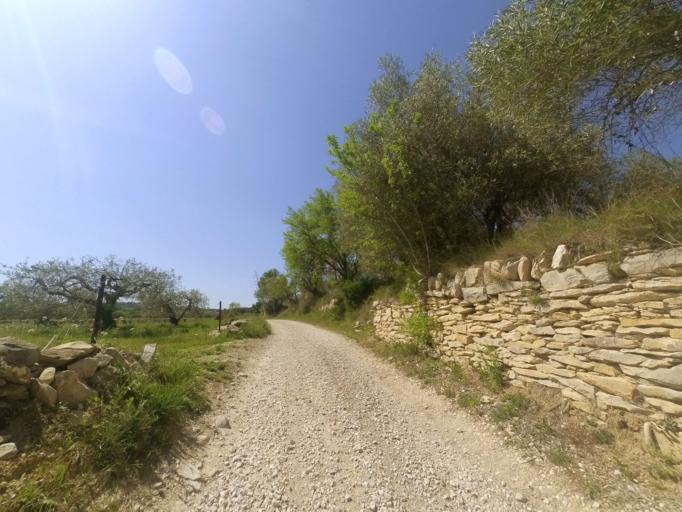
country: FR
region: Languedoc-Roussillon
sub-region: Departement du Gard
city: Congenies
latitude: 43.7782
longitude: 4.1725
